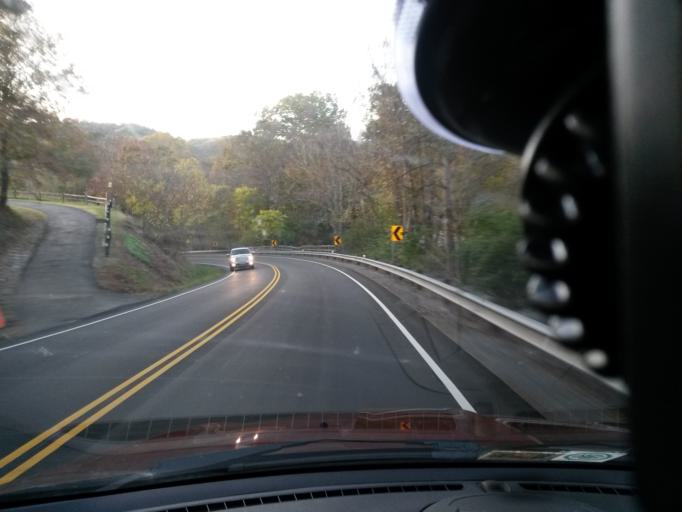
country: US
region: Virginia
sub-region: Roanoke County
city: Vinton
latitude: 37.2186
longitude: -79.8918
